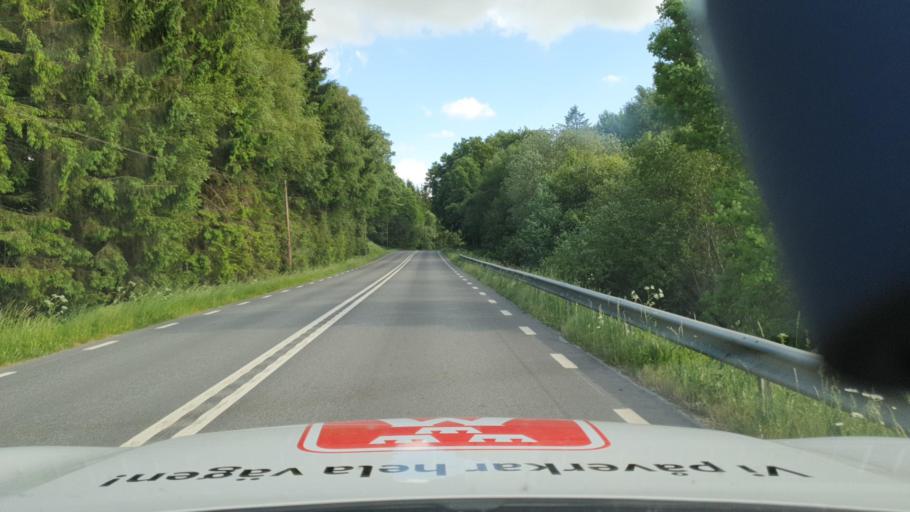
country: SE
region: Skane
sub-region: Simrishamns Kommun
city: Kivik
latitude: 55.6091
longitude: 14.1415
